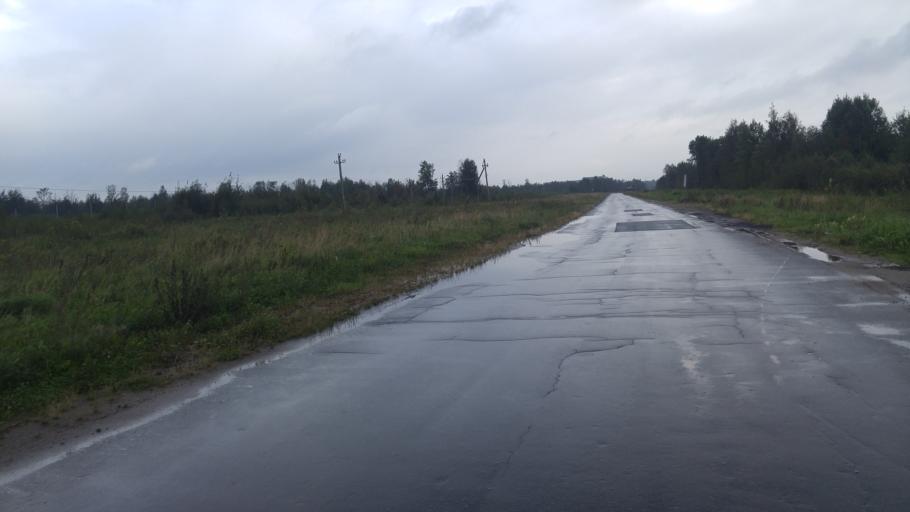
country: RU
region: St.-Petersburg
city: Metallostroy
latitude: 59.7816
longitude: 30.5712
